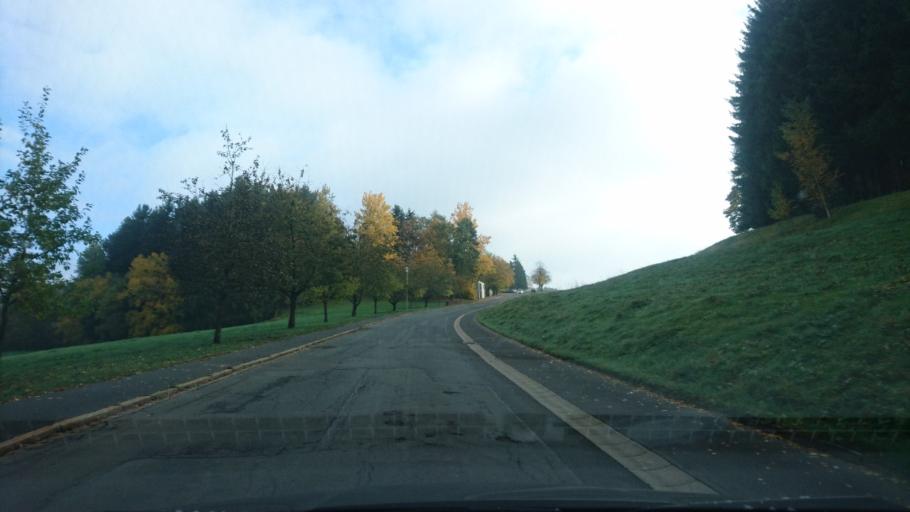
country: DE
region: Bavaria
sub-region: Upper Franconia
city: Selbitz
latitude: 50.3152
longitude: 11.7538
